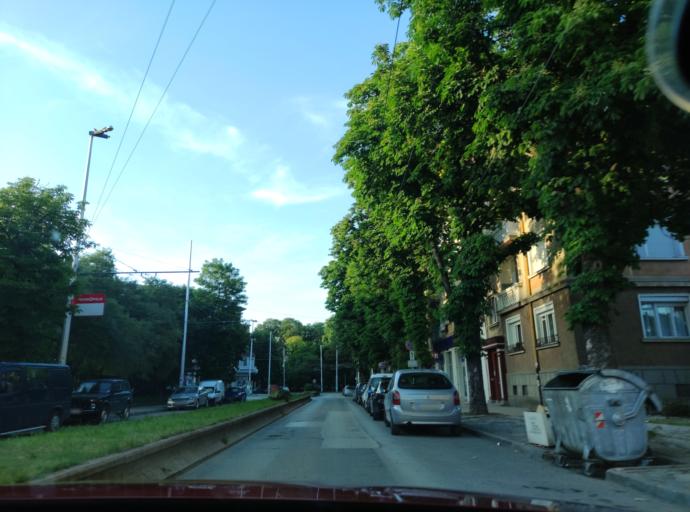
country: BG
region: Pleven
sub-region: Obshtina Pleven
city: Pleven
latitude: 43.4180
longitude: 24.6137
